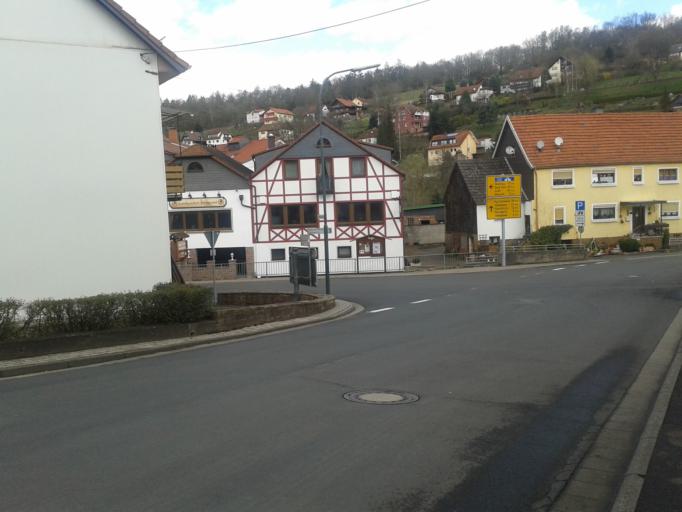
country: DE
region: Bavaria
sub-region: Regierungsbezirk Unterfranken
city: Obersinn
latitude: 50.2379
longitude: 9.5934
